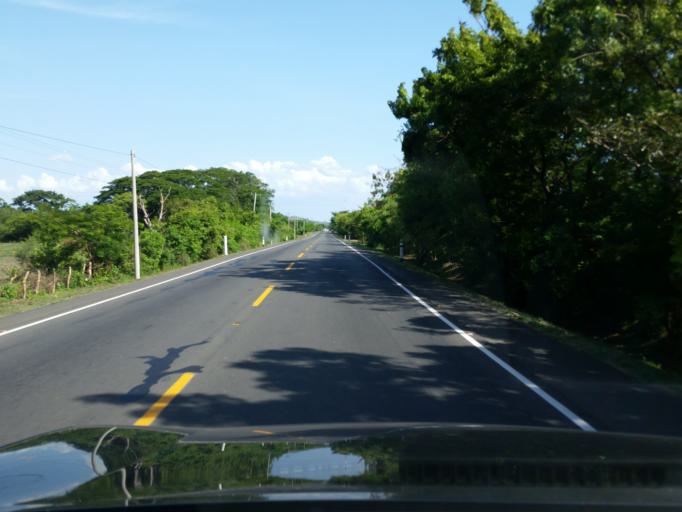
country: NI
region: Leon
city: Leon
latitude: 12.3809
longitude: -86.8408
